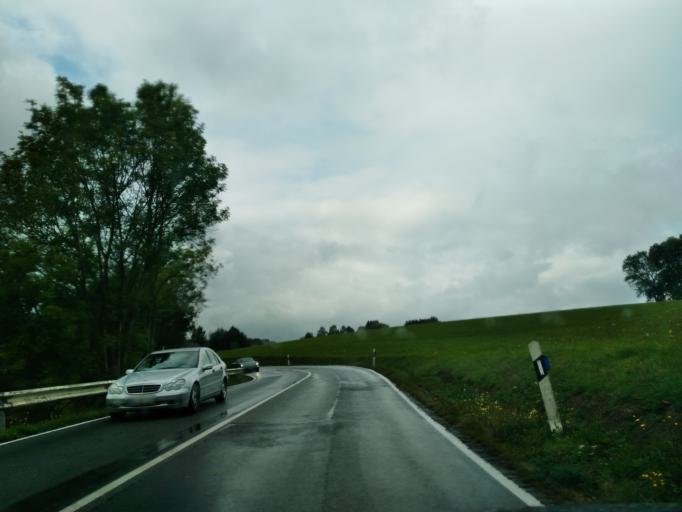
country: DE
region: Rheinland-Pfalz
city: Asbach
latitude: 50.6663
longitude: 7.3857
